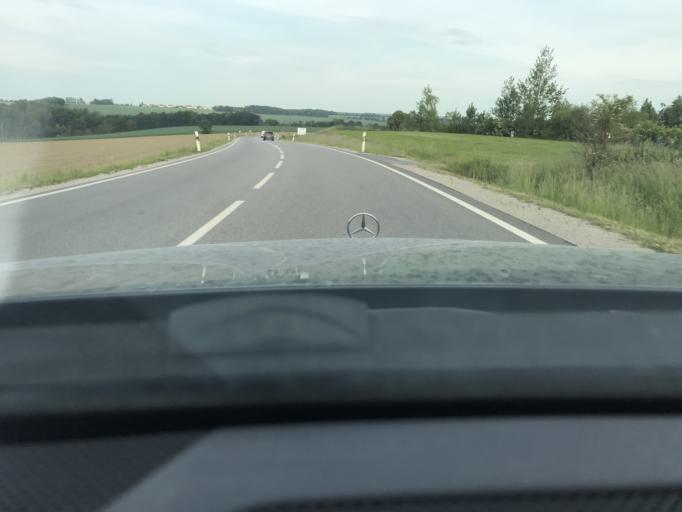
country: DE
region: Saxony
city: Dennheritz
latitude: 50.8168
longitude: 12.4383
